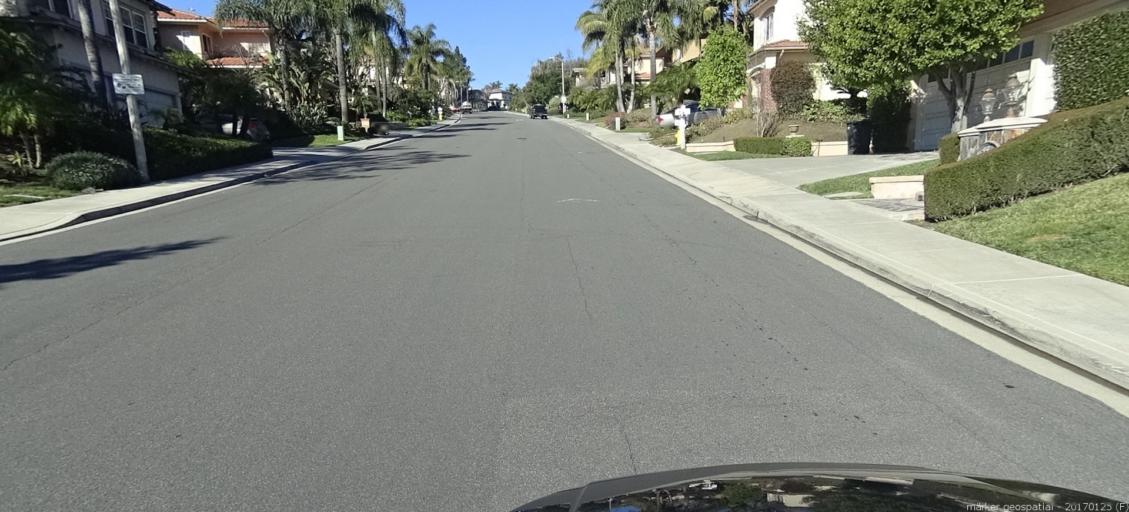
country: US
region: California
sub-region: Orange County
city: Portola Hills
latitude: 33.6764
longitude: -117.6355
